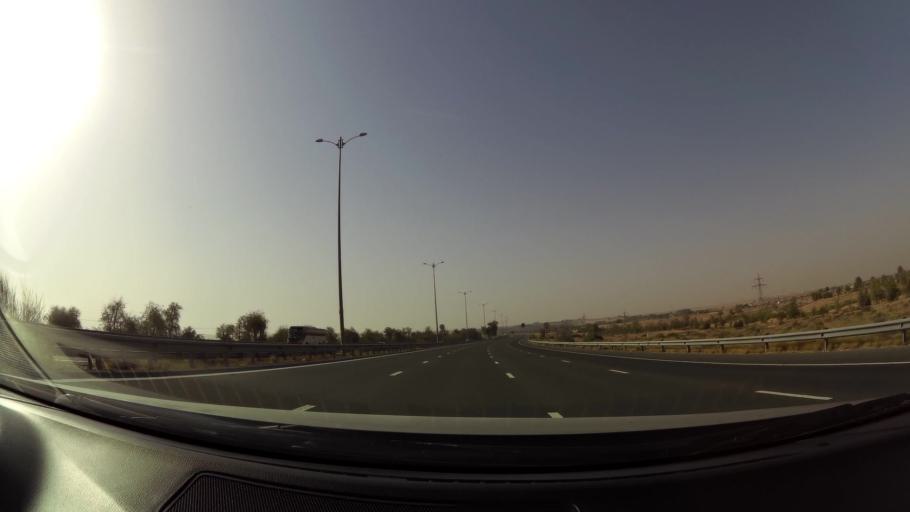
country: OM
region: Al Buraimi
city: Al Buraymi
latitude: 24.6504
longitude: 55.7030
